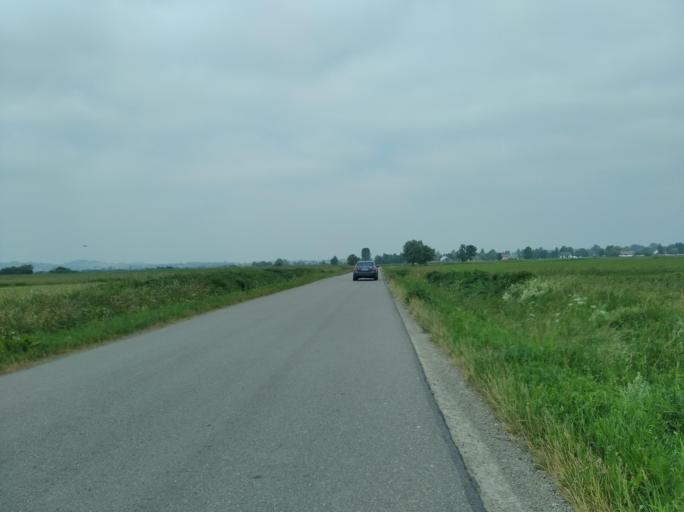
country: PL
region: Subcarpathian Voivodeship
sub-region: Powiat sanocki
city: Besko
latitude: 49.6119
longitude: 21.9537
